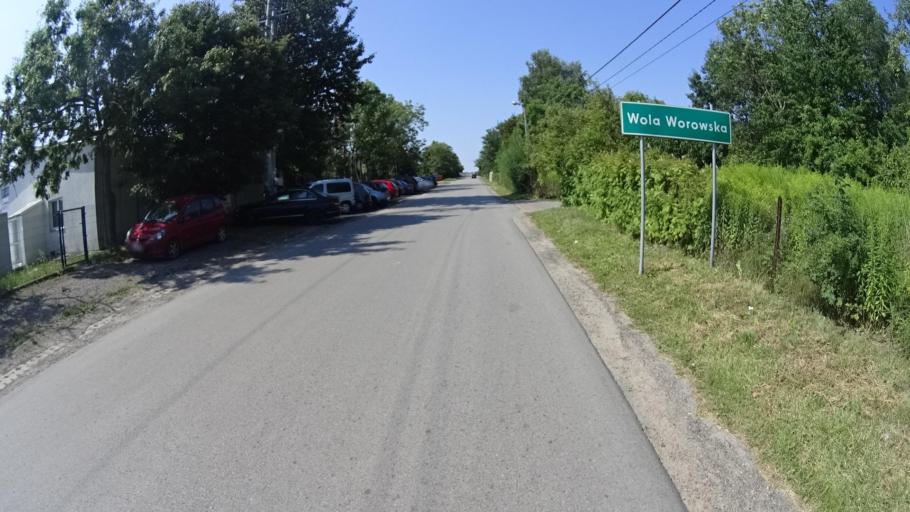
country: PL
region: Masovian Voivodeship
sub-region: Powiat grojecki
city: Grojec
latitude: 51.8874
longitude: 20.8608
